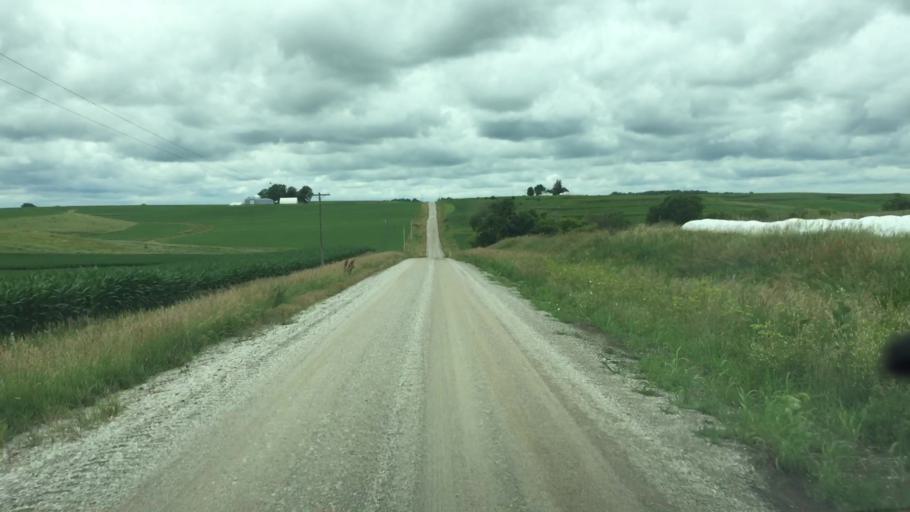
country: US
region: Iowa
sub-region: Jasper County
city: Monroe
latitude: 41.6010
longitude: -93.1225
